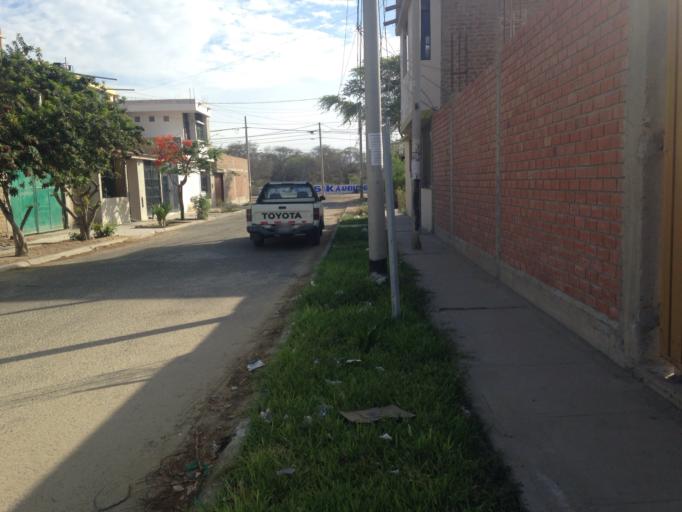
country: PE
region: Piura
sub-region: Provincia de Piura
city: Piura
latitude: -5.1753
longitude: -80.6422
